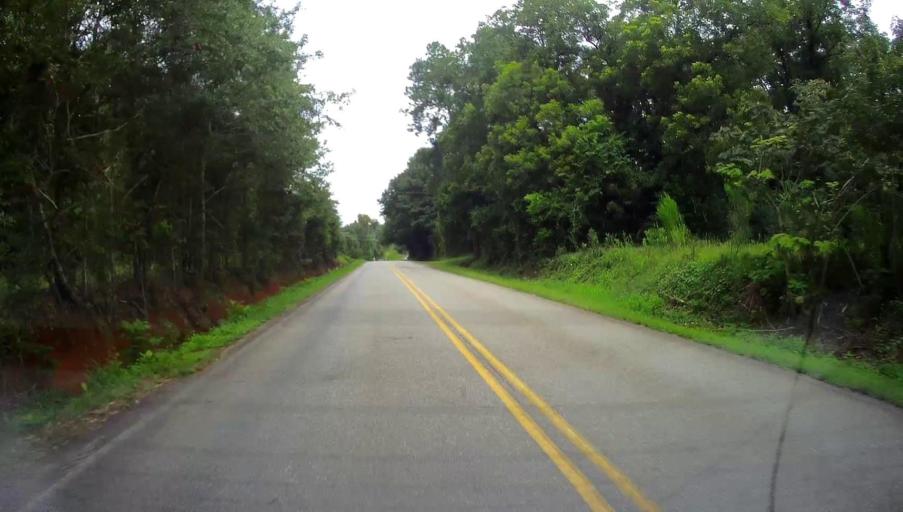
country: US
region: Georgia
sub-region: Peach County
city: Byron
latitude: 32.5844
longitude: -83.7484
